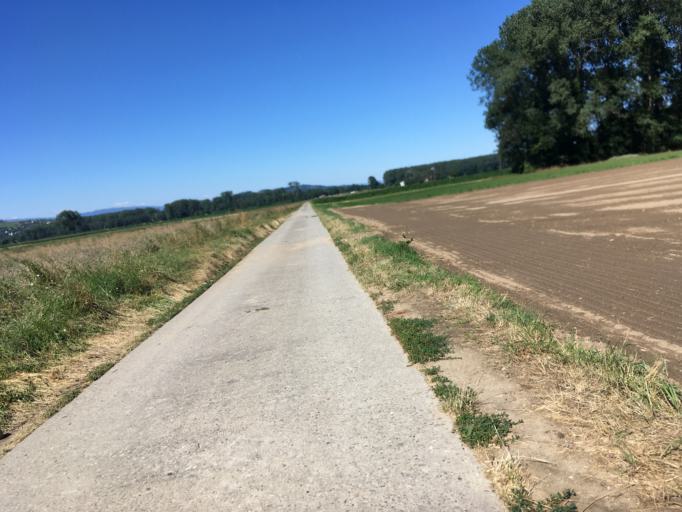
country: CH
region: Vaud
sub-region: Broye-Vully District
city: Avenches
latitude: 46.8980
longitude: 7.0262
